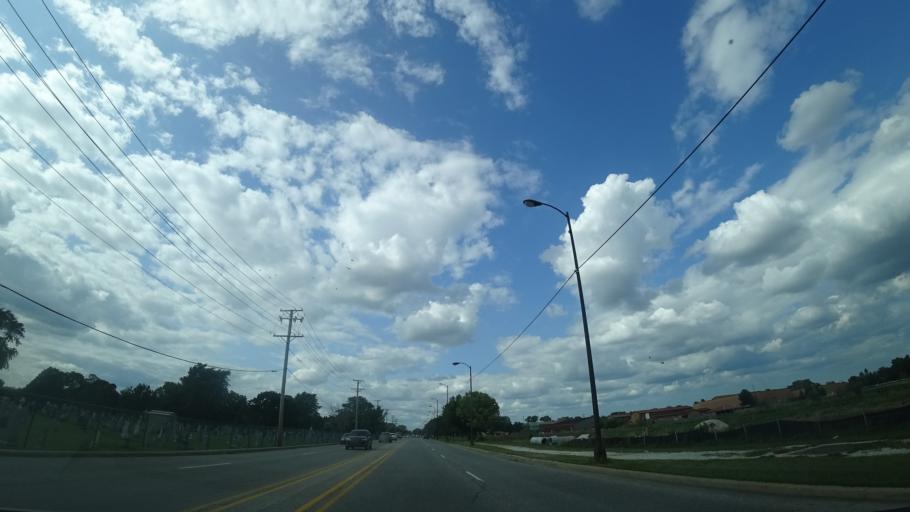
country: US
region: Illinois
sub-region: Cook County
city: Merrionette Park
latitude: 41.6881
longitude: -87.7202
